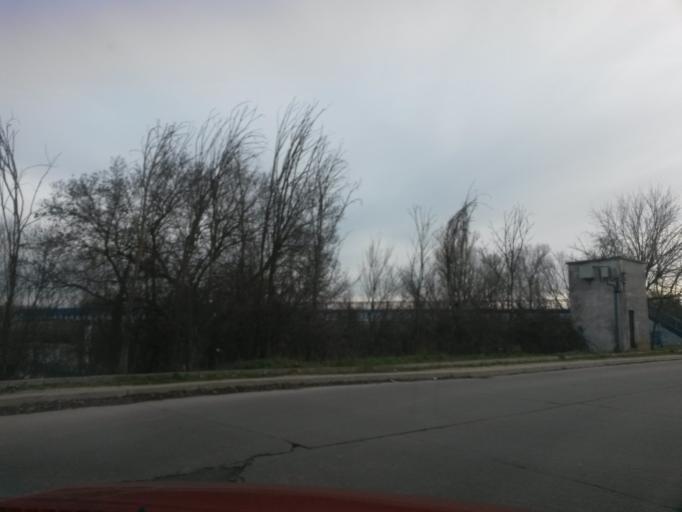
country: ES
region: Castille and Leon
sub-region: Provincia de Salamanca
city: Cabrerizos
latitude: 40.9683
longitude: -5.6213
